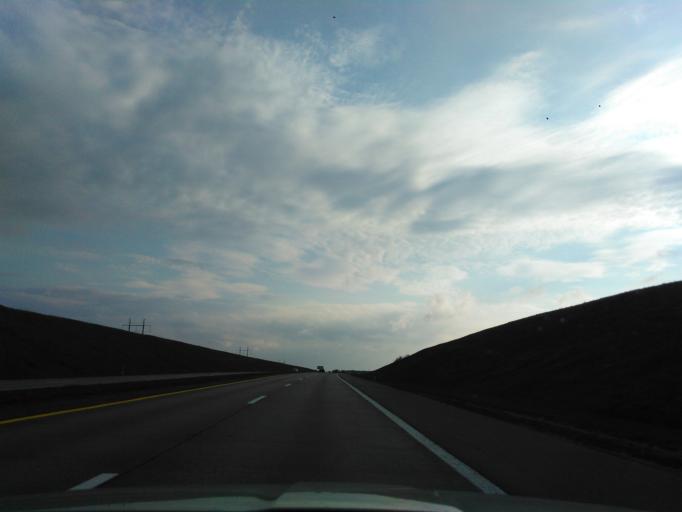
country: BY
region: Minsk
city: Astrashytski Haradok
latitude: 54.0999
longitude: 27.7908
